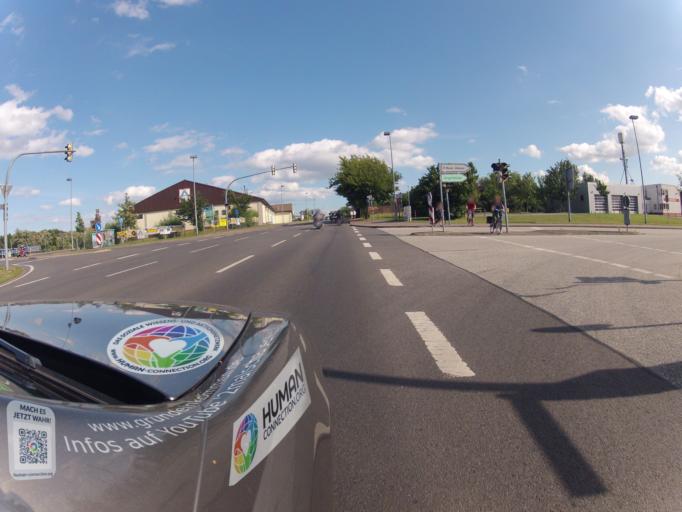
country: DE
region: Mecklenburg-Vorpommern
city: Loddin
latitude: 54.0152
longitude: 14.0464
